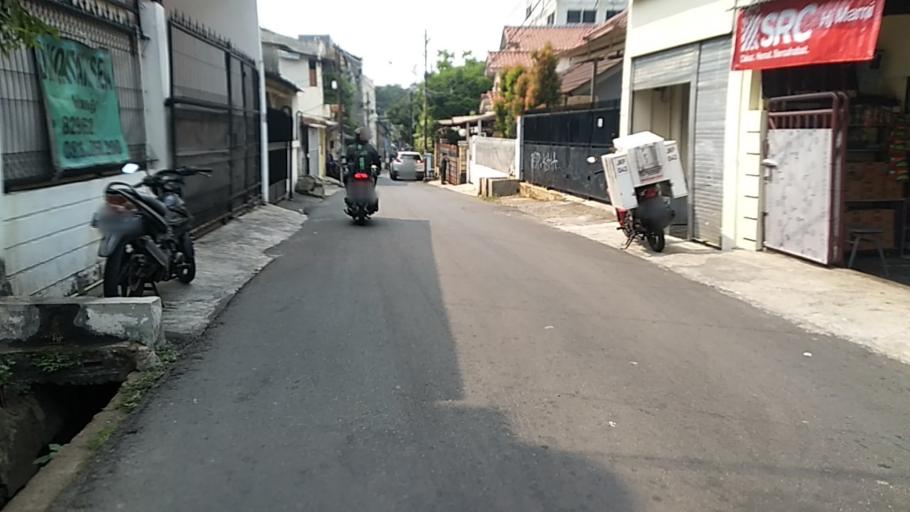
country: ID
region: Jakarta Raya
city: Jakarta
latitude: -6.2241
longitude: 106.8500
